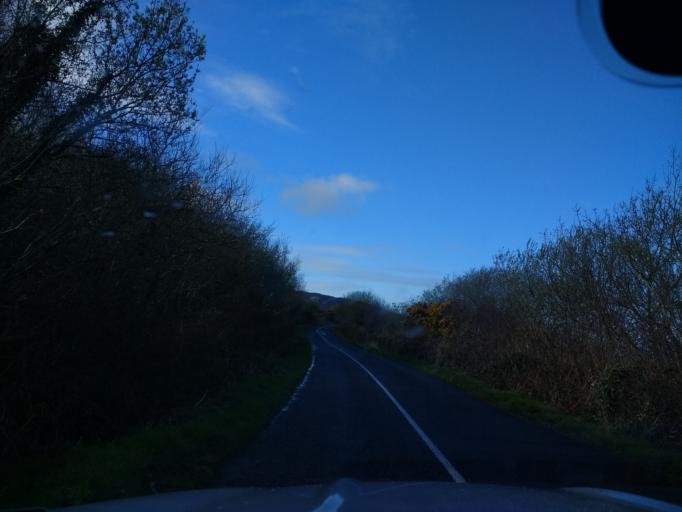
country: IE
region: Ulster
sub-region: County Donegal
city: Buncrana
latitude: 55.1628
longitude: -7.5679
